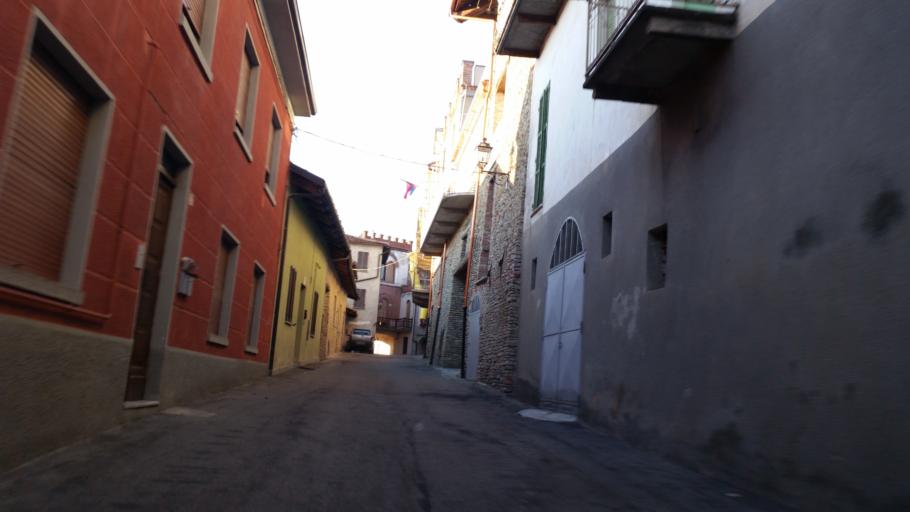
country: IT
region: Piedmont
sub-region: Provincia di Cuneo
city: Mango
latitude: 44.6851
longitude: 8.1491
